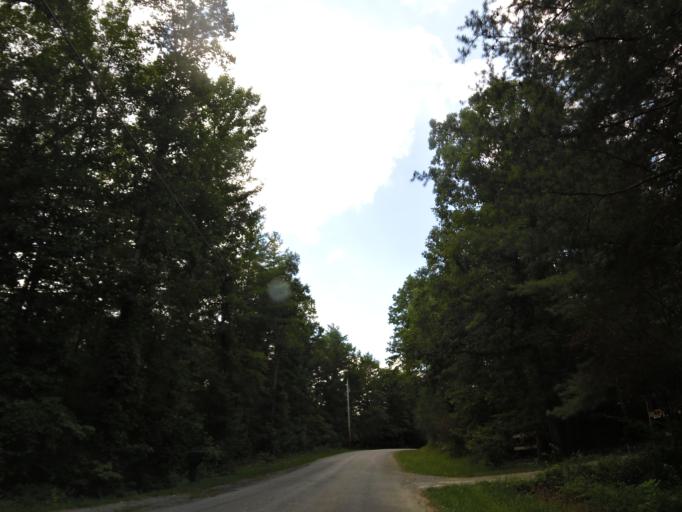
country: US
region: Tennessee
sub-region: Roane County
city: Rockwood
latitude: 35.8892
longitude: -84.7839
